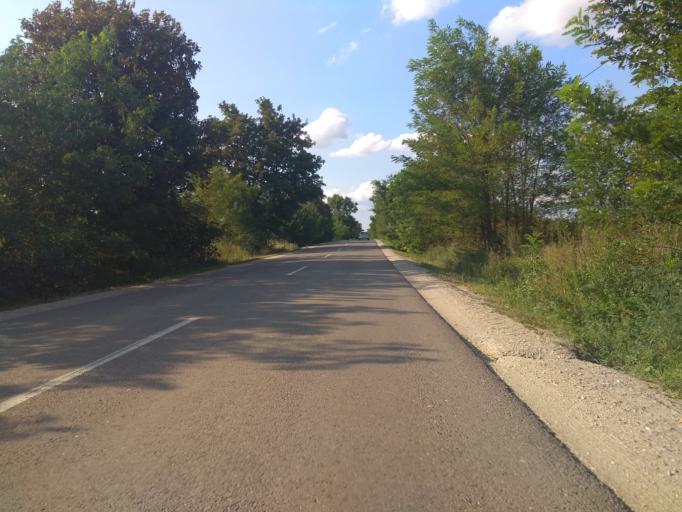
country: HU
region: Borsod-Abauj-Zemplen
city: Hejobaba
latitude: 47.8945
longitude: 20.8932
